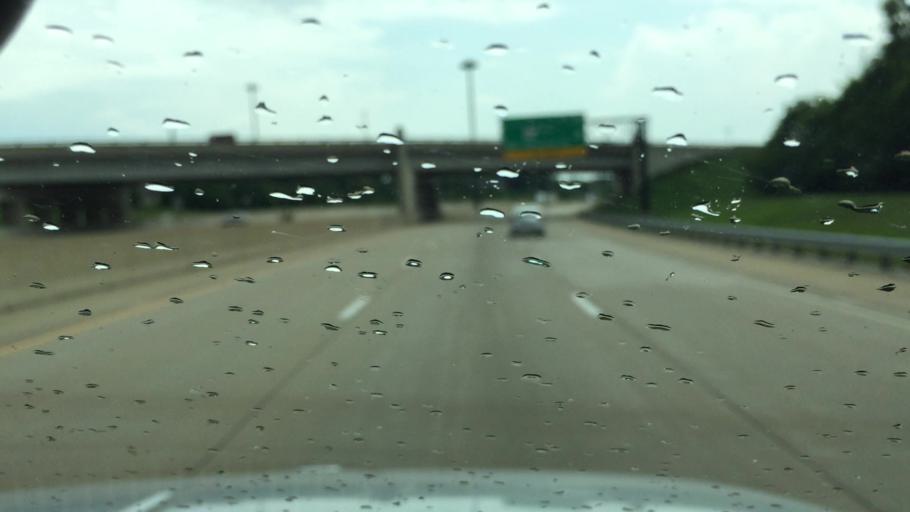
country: US
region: Illinois
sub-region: Peoria County
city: West Peoria
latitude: 40.7355
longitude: -89.6249
